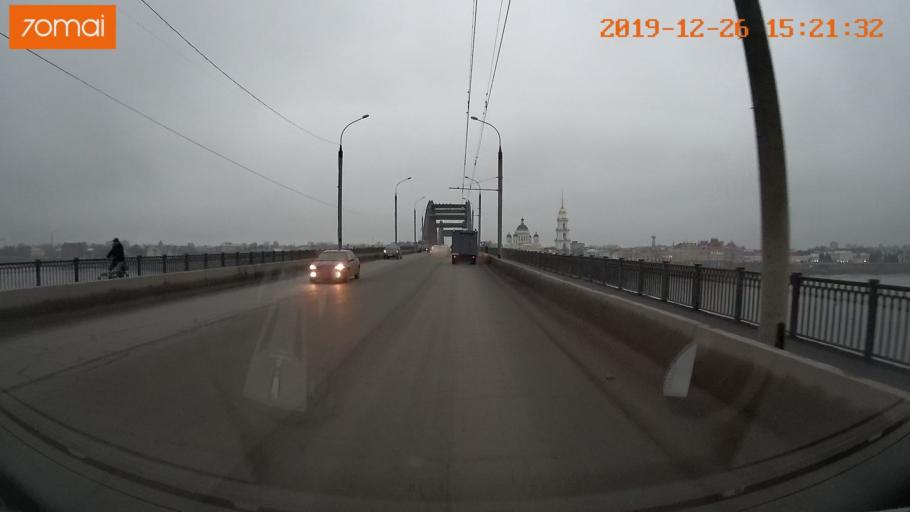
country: RU
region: Jaroslavl
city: Rybinsk
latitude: 58.0528
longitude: 38.8632
